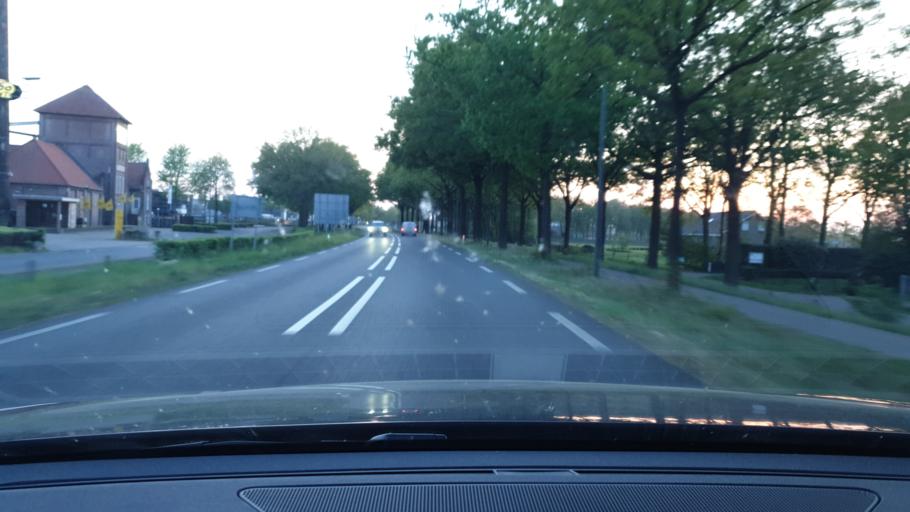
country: NL
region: North Brabant
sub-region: Gemeente Bladel en Netersel
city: Bladel
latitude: 51.3619
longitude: 5.2023
